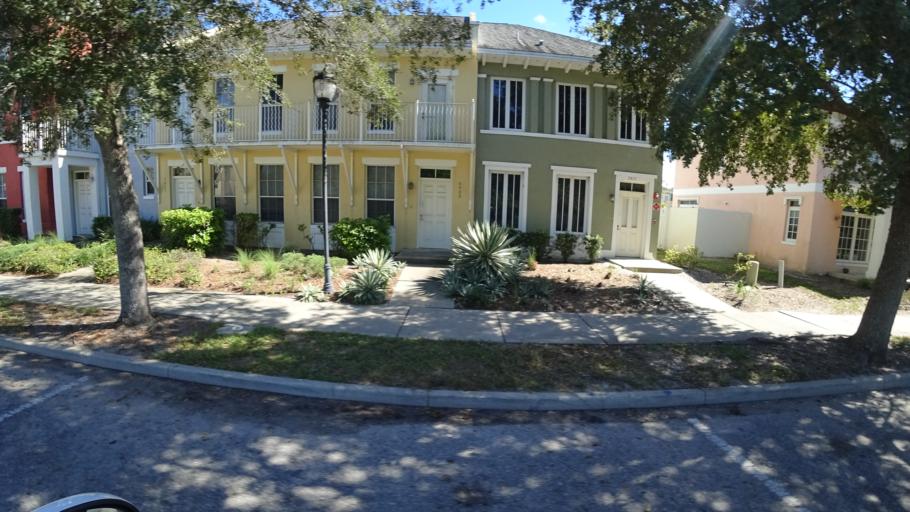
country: US
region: Florida
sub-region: Manatee County
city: Bradenton
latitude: 27.4872
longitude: -82.5654
